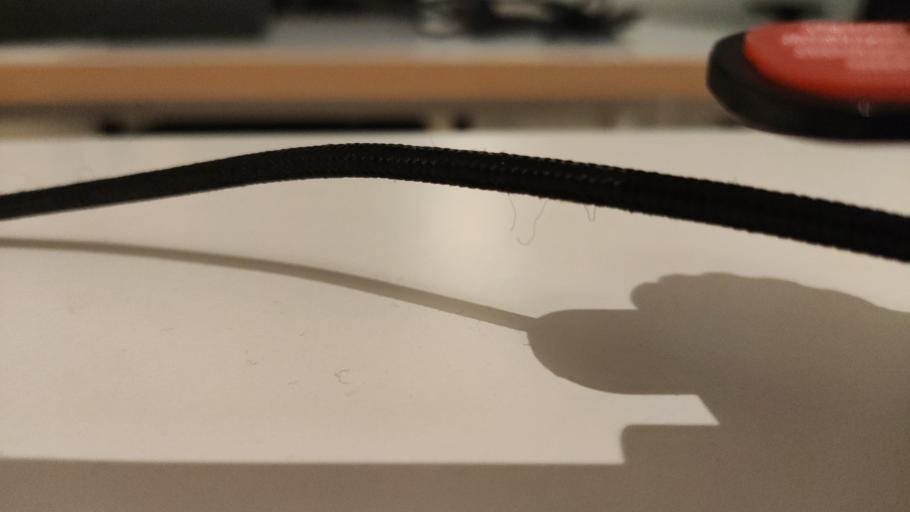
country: RU
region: Moskovskaya
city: Orekhovo-Zuyevo
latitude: 55.8222
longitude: 38.9656
